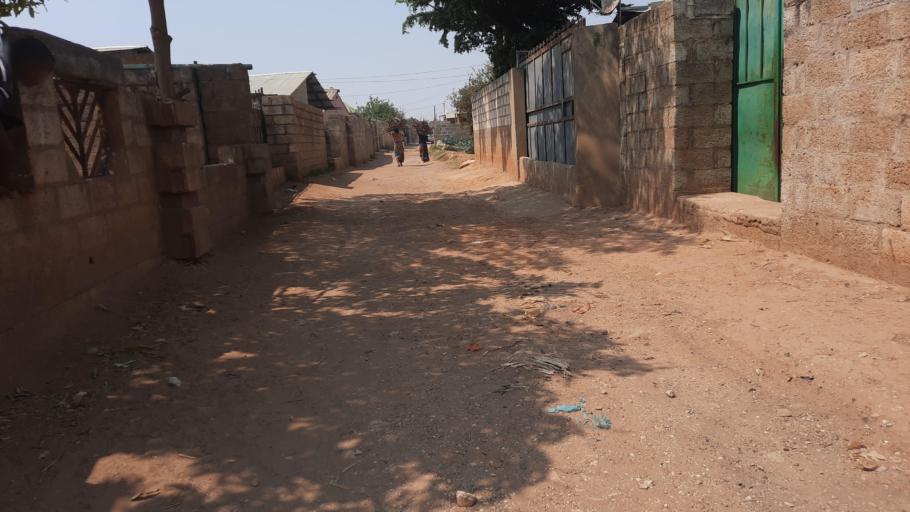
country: ZM
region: Lusaka
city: Lusaka
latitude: -15.3929
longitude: 28.3815
